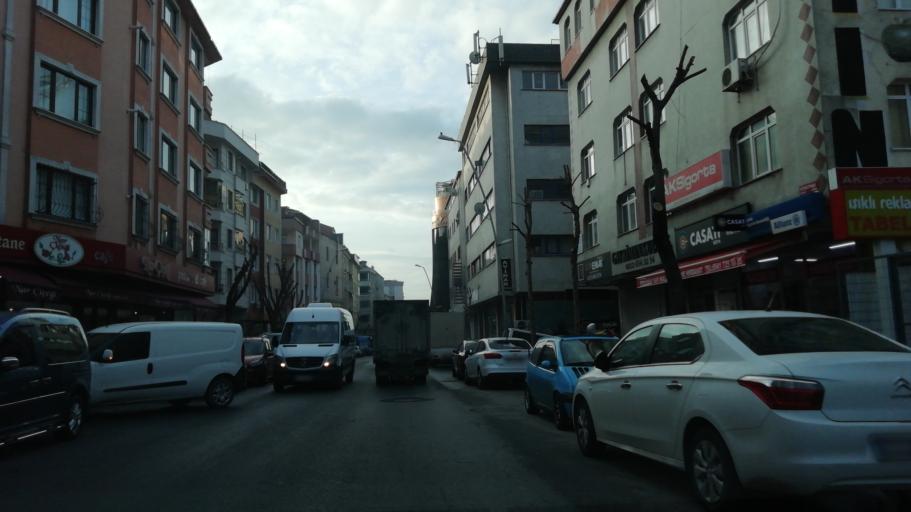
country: TR
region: Istanbul
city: Bahcelievler
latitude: 41.0029
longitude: 28.8266
